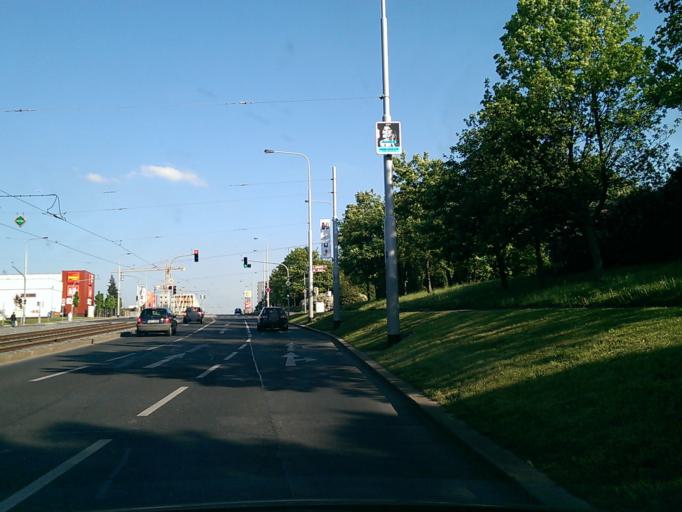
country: CZ
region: Praha
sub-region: Praha 9
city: Vysocany
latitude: 50.0587
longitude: 14.5099
